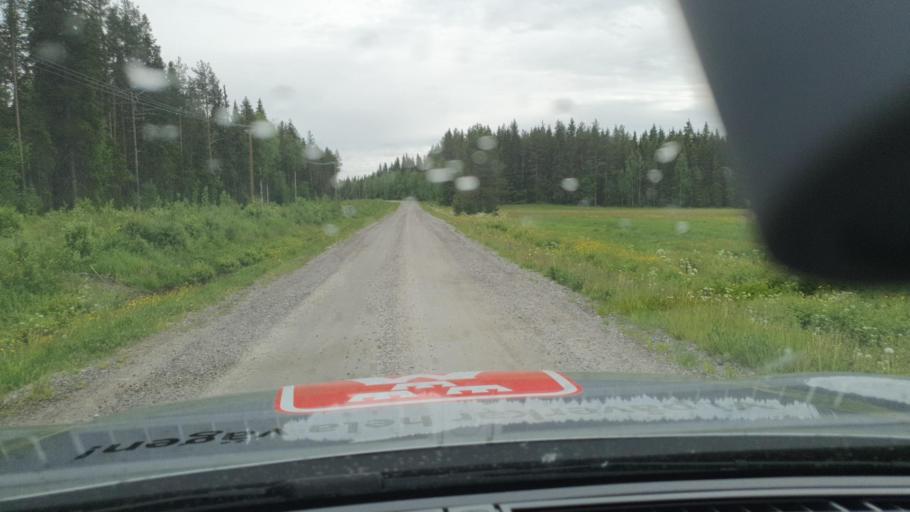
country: SE
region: Norrbotten
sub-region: Kalix Kommun
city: Rolfs
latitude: 66.0416
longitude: 23.0516
